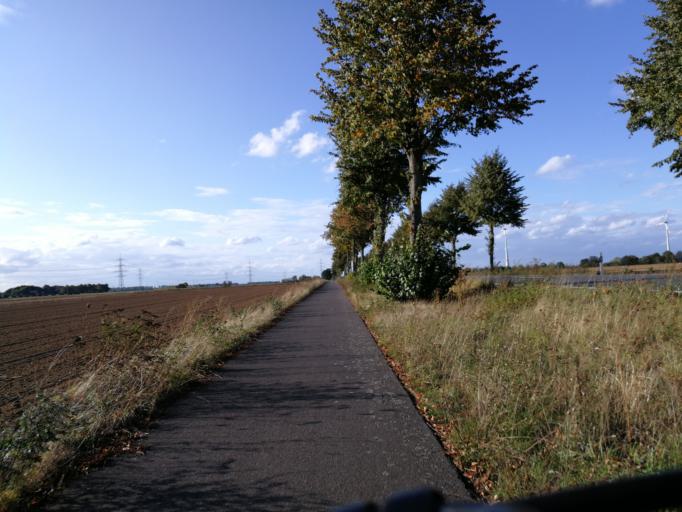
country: DE
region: North Rhine-Westphalia
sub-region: Regierungsbezirk Dusseldorf
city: Neubrueck
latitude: 51.1182
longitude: 6.7089
